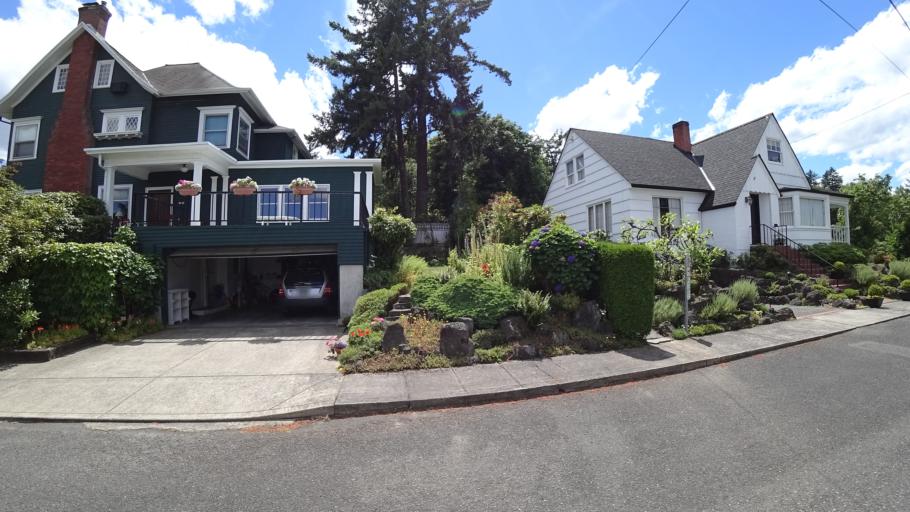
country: US
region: Oregon
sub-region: Multnomah County
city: Portland
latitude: 45.5124
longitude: -122.6936
